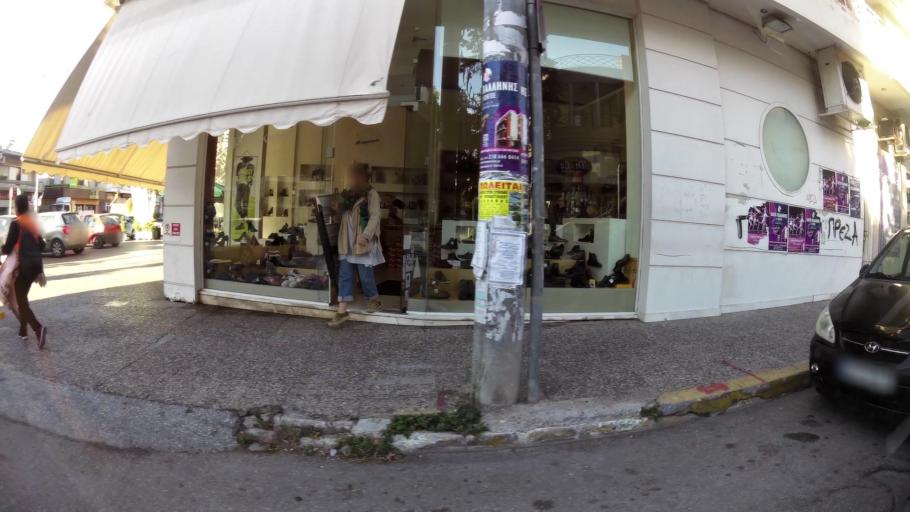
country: GR
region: Attica
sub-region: Nomarchia Anatolikis Attikis
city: Pallini
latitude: 38.0039
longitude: 23.8809
